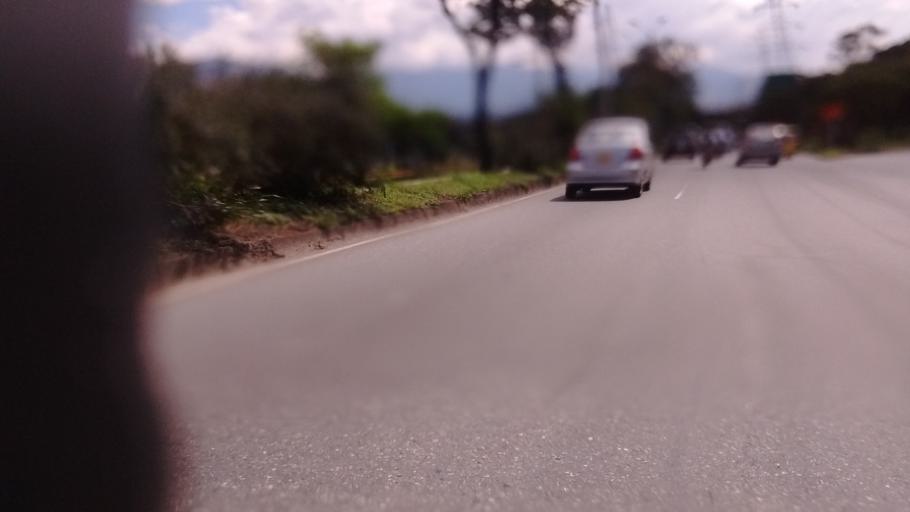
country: CO
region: Antioquia
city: Itagui
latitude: 6.2154
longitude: -75.5782
